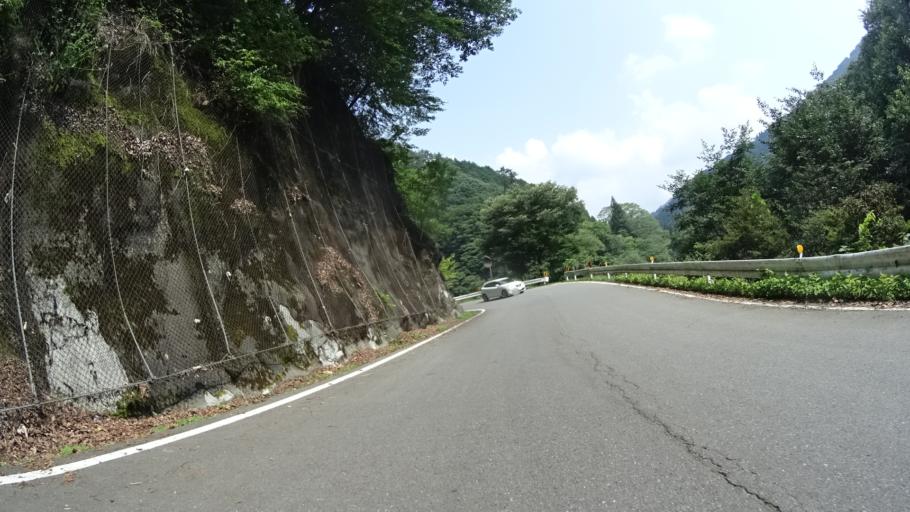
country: JP
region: Gunma
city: Tomioka
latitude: 36.0612
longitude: 138.8320
